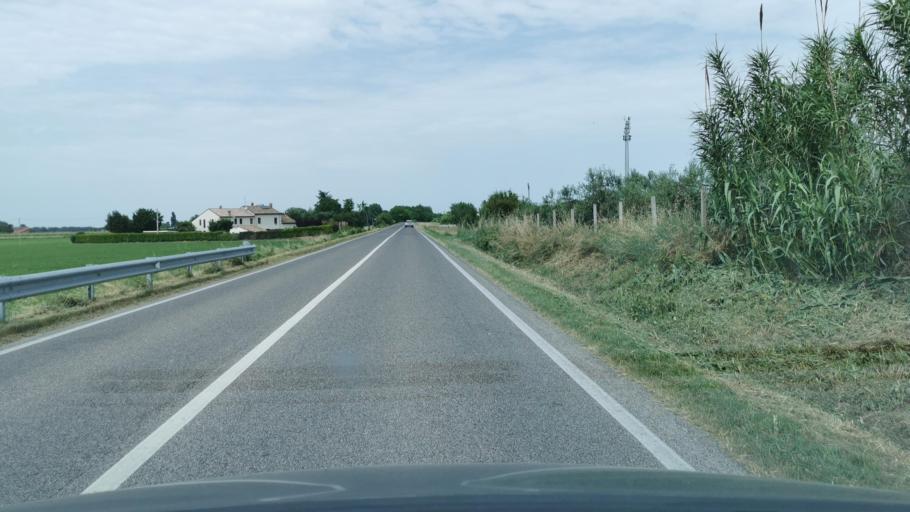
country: IT
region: Emilia-Romagna
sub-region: Provincia di Ravenna
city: Savarna-Conventella
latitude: 44.5109
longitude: 12.1005
